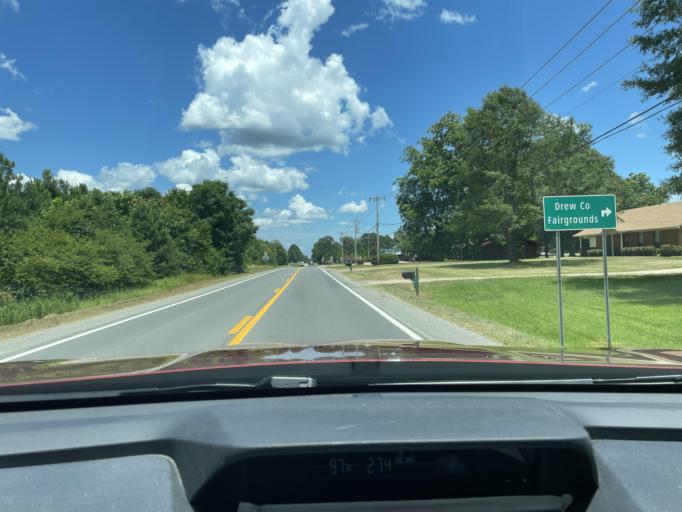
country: US
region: Arkansas
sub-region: Drew County
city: Monticello
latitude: 33.6287
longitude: -91.7611
